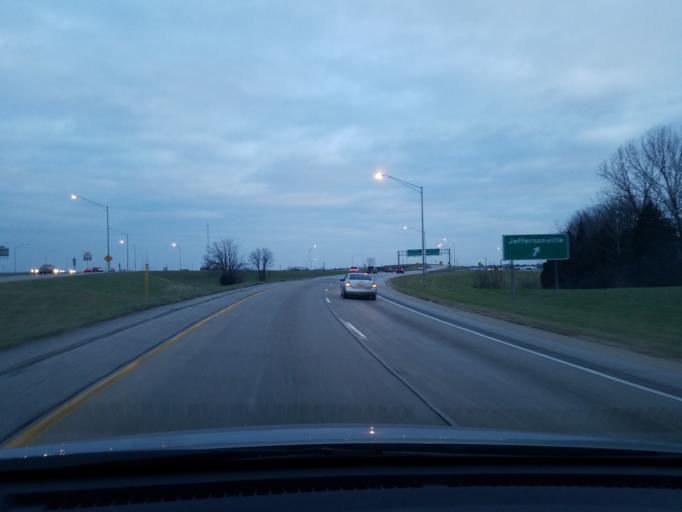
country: US
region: Indiana
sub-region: Clark County
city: Clarksville
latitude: 38.3454
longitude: -85.7586
